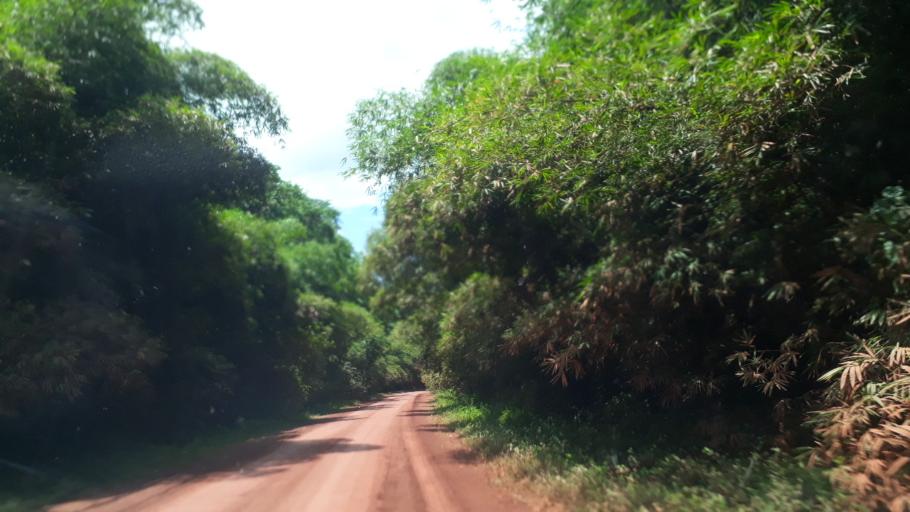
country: CD
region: Eastern Province
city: Kisangani
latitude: 0.6076
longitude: 26.0096
